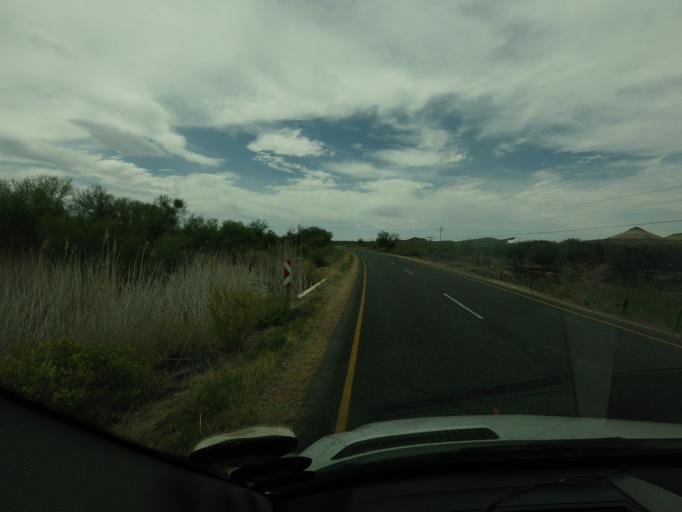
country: ZA
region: Western Cape
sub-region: Overberg District Municipality
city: Swellendam
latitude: -33.8507
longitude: 20.8504
